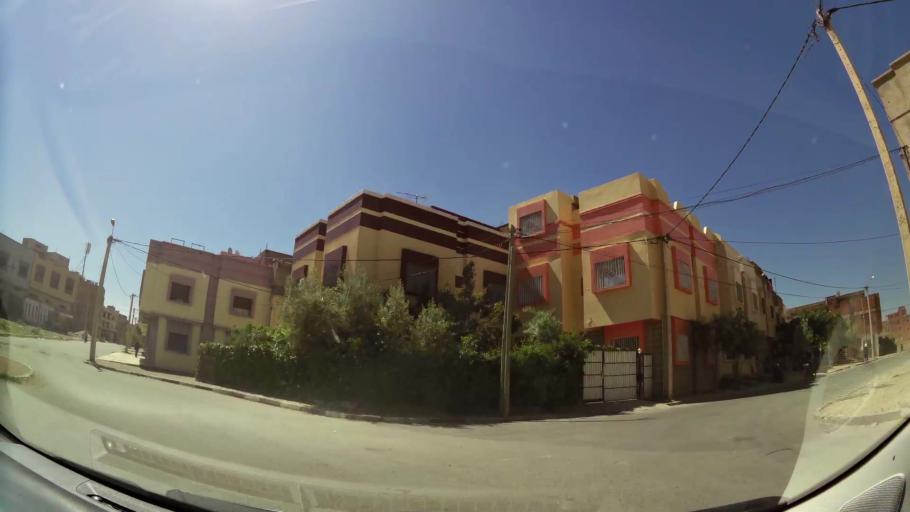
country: MA
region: Oriental
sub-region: Oujda-Angad
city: Oujda
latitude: 34.6574
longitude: -1.8760
